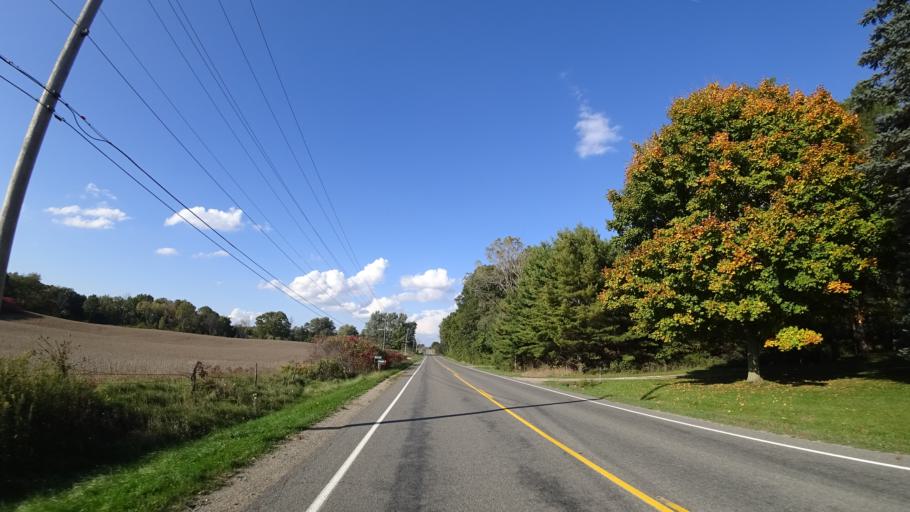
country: US
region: Michigan
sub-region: Saint Joseph County
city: Centreville
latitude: 41.8716
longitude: -85.5068
